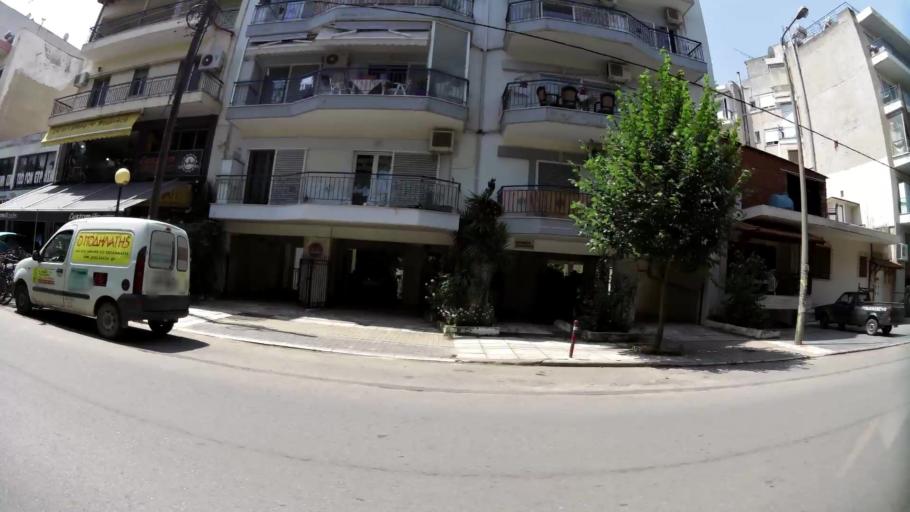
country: GR
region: Central Macedonia
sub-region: Nomos Thessalonikis
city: Evosmos
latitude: 40.6717
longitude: 22.9000
